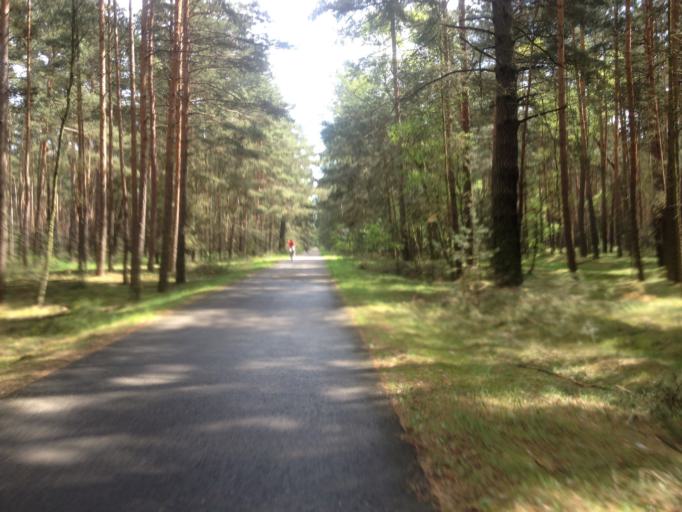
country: DE
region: Brandenburg
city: Briesen
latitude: 51.8071
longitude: 14.2682
